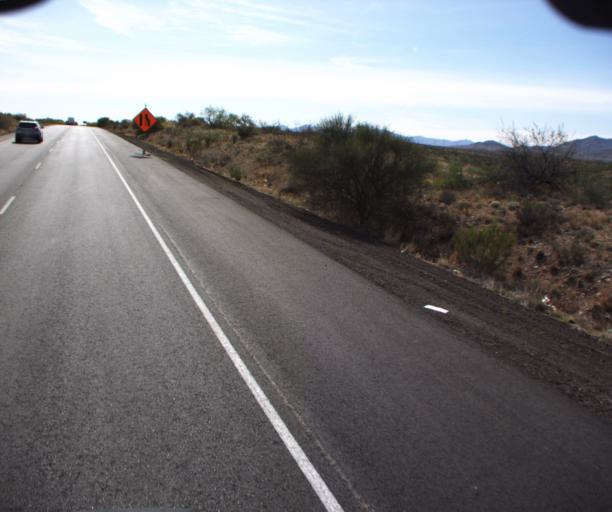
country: US
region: Arizona
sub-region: Pima County
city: Vail
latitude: 31.9990
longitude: -110.6694
